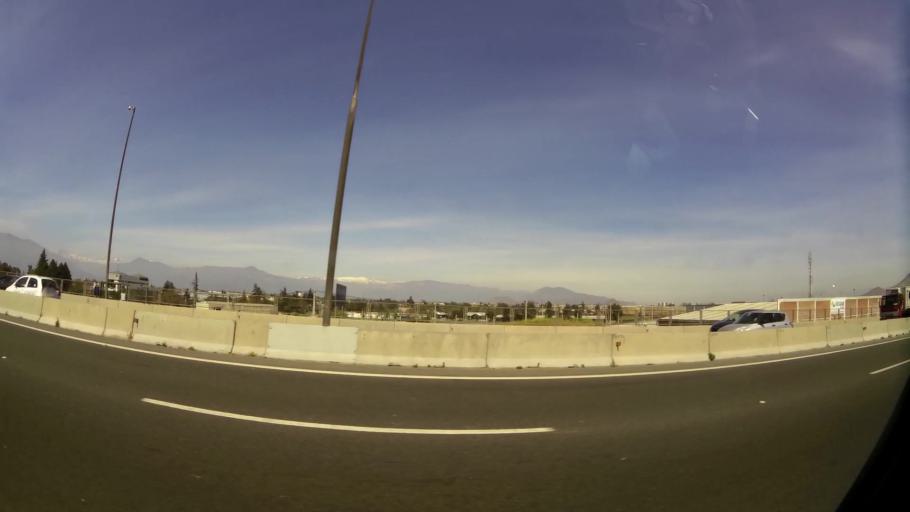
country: CL
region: Santiago Metropolitan
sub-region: Provincia de Maipo
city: San Bernardo
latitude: -33.5455
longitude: -70.6934
